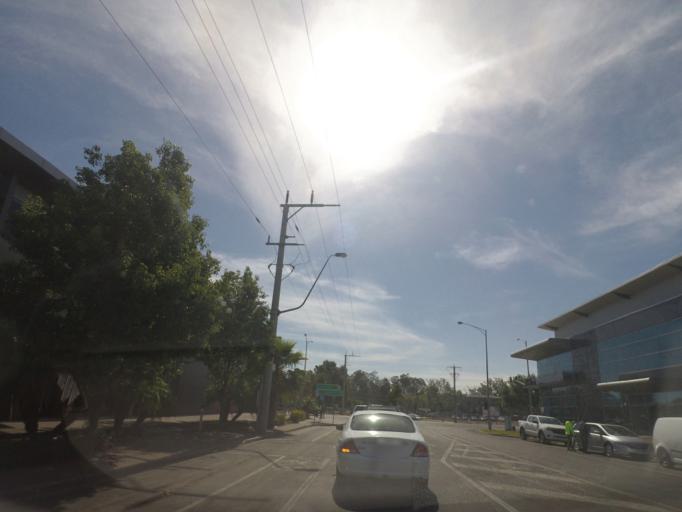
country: AU
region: Victoria
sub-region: Greater Shepparton
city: Shepparton
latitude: -36.3853
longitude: 145.3992
